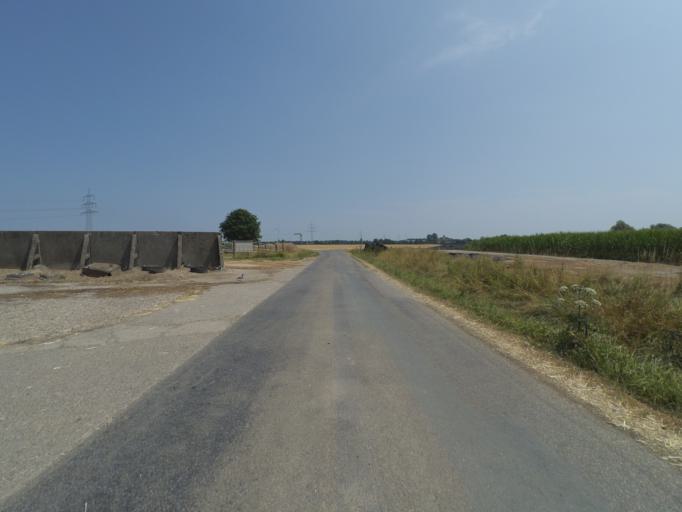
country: DE
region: North Rhine-Westphalia
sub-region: Regierungsbezirk Dusseldorf
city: Mehrhoog
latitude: 51.7405
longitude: 6.4694
